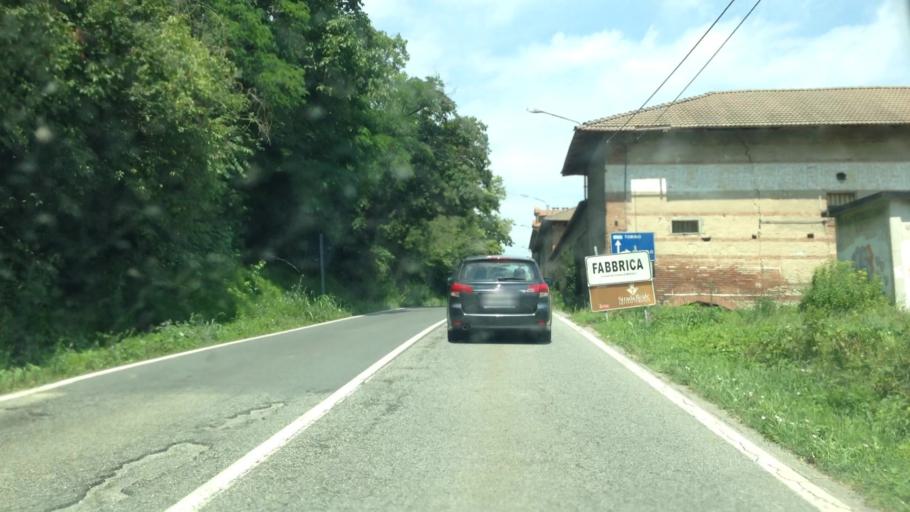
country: IT
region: Piedmont
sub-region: Provincia di Torino
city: Brozolo
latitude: 45.1116
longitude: 8.0695
